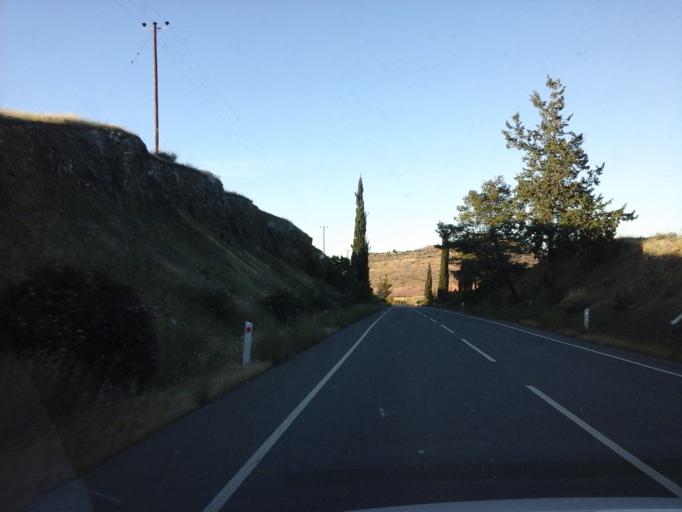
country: CY
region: Lefkosia
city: Kakopetria
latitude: 35.0802
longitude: 32.9490
